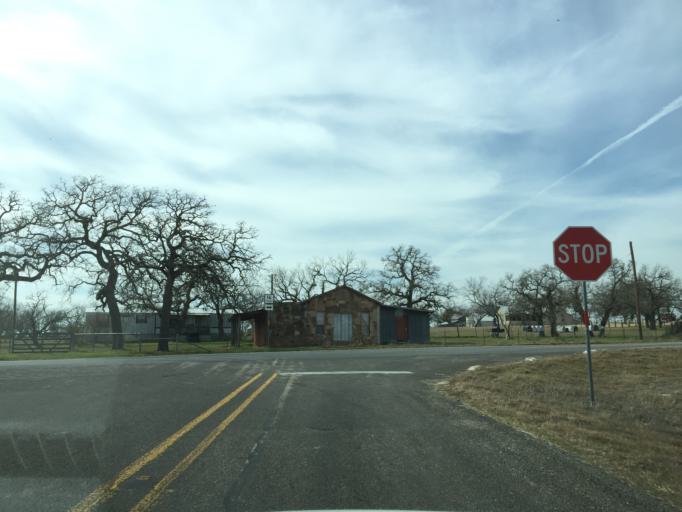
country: US
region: Texas
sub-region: Gillespie County
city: Fredericksburg
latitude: 30.4134
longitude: -98.7364
